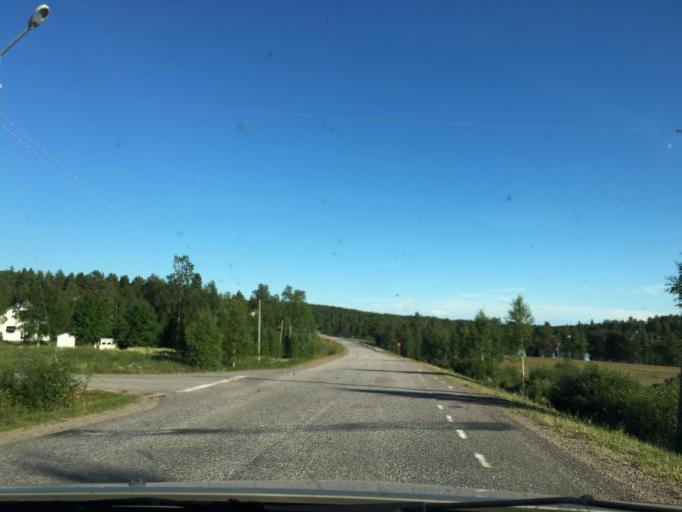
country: SE
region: Norrbotten
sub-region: Kalix Kommun
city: Rolfs
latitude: 65.9196
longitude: 22.9153
